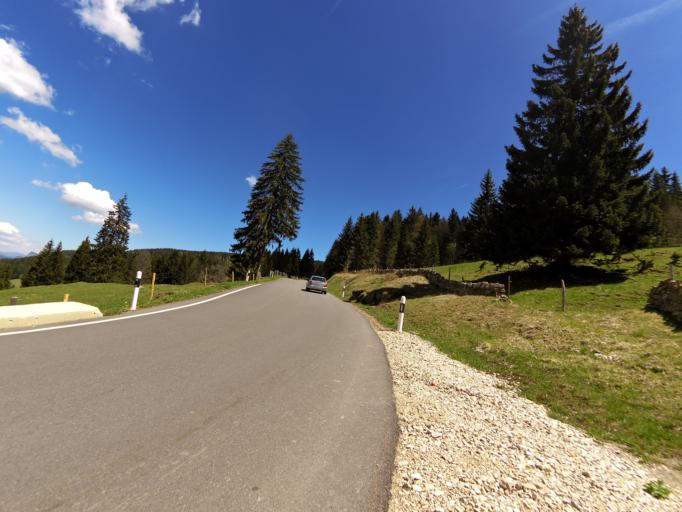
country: CH
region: Vaud
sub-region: Jura-Nord vaudois District
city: Le Chenit
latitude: 46.5732
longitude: 6.2087
